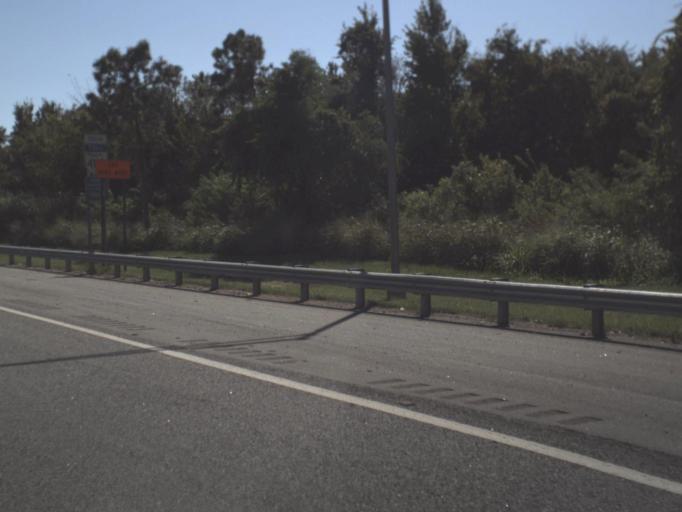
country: US
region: Florida
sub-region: Seminole County
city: Sanford
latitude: 28.7654
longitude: -81.2724
